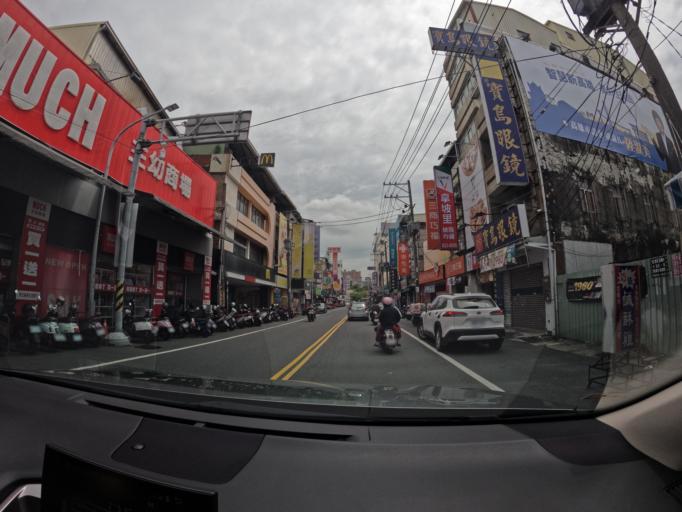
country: TW
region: Kaohsiung
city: Kaohsiung
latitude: 22.7943
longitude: 120.2908
